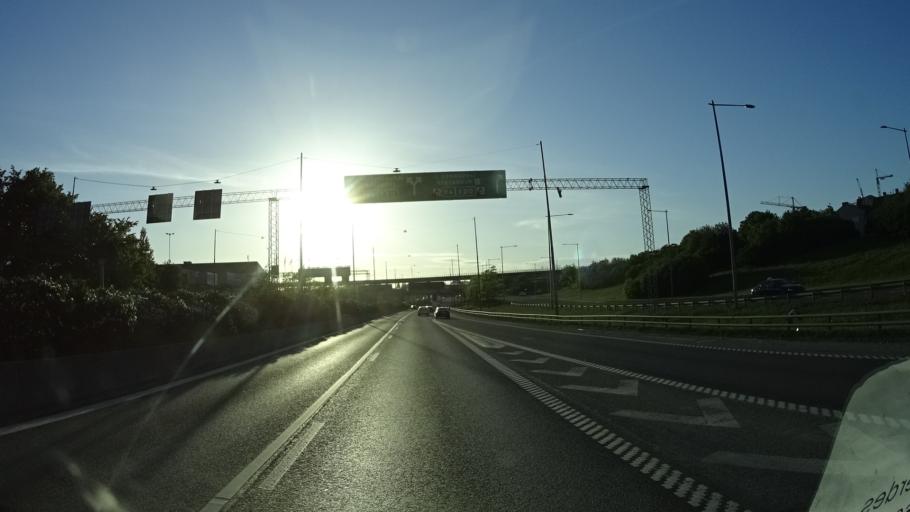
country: SE
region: Stockholm
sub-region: Stockholms Kommun
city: Arsta
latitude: 59.2943
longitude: 18.0407
